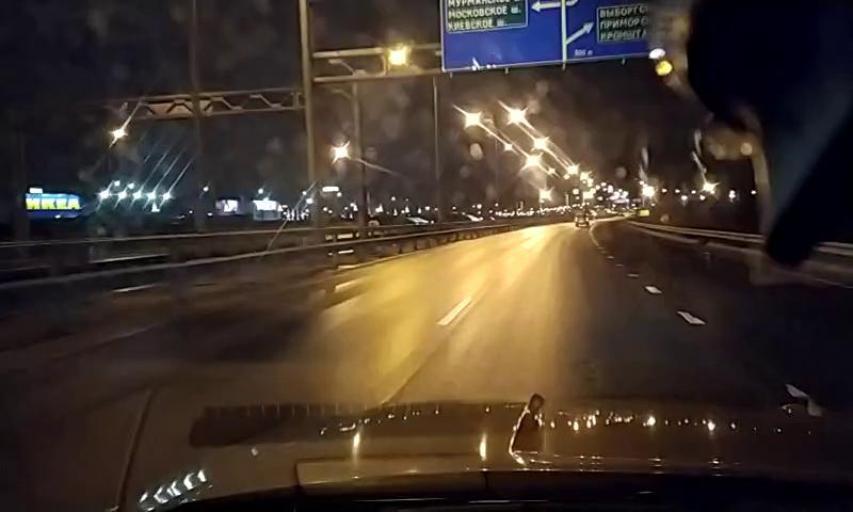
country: RU
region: Leningrad
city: Bugry
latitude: 60.0965
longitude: 30.3790
